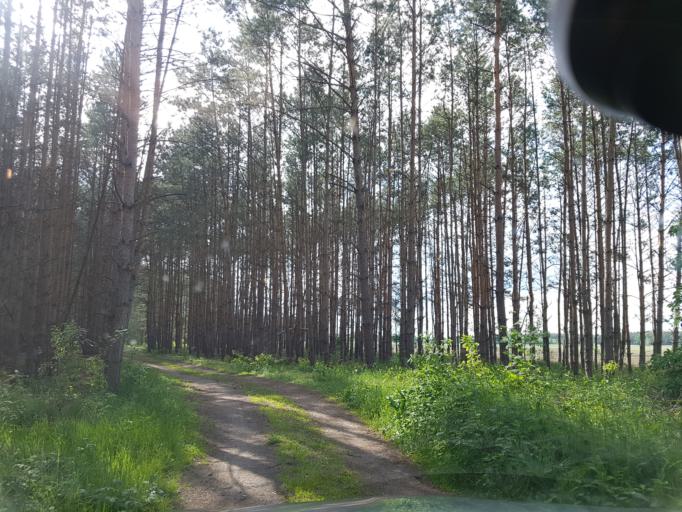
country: DE
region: Brandenburg
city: Schonewalde
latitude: 51.6366
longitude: 13.6250
